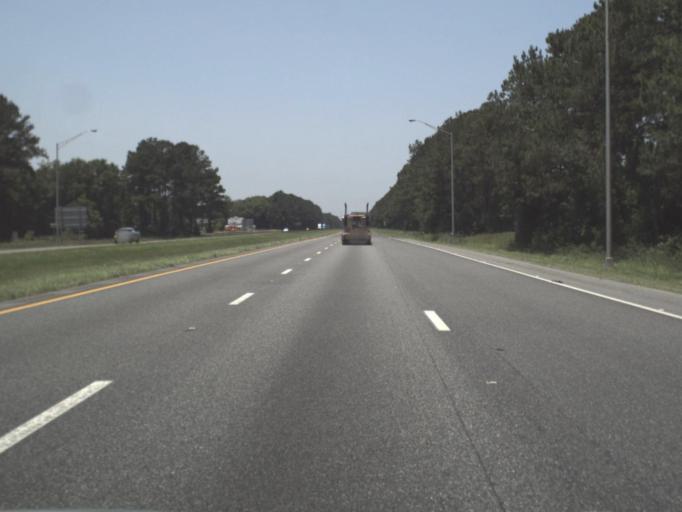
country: US
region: Florida
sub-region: Baker County
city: Macclenny
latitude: 30.2593
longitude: -82.1267
